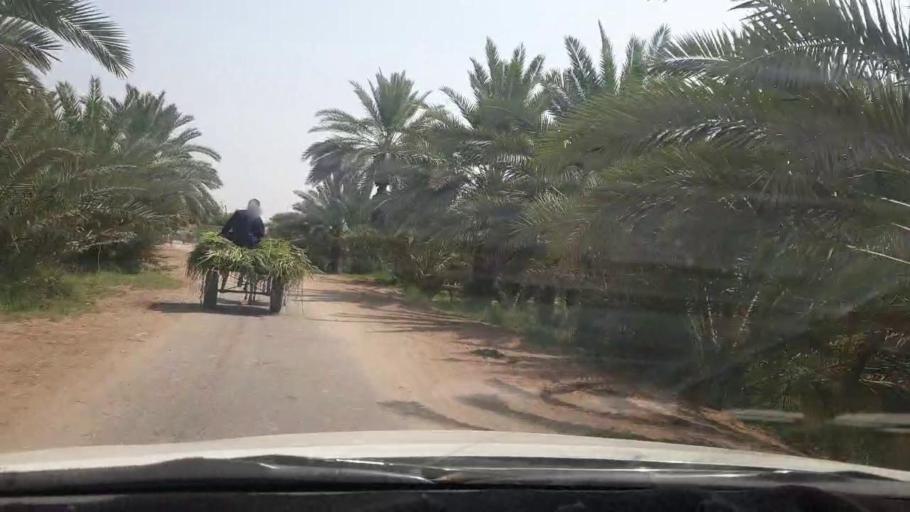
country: PK
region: Sindh
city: Rohri
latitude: 27.5994
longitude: 68.9058
